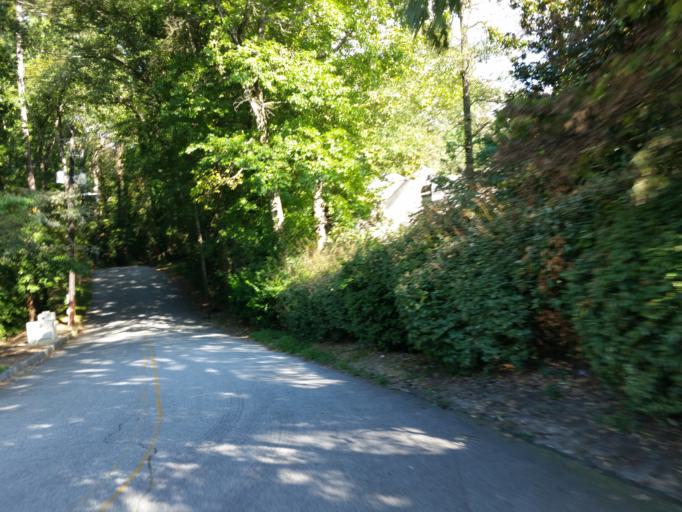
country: US
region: Georgia
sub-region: Cobb County
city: Vinings
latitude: 33.8666
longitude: -84.4374
